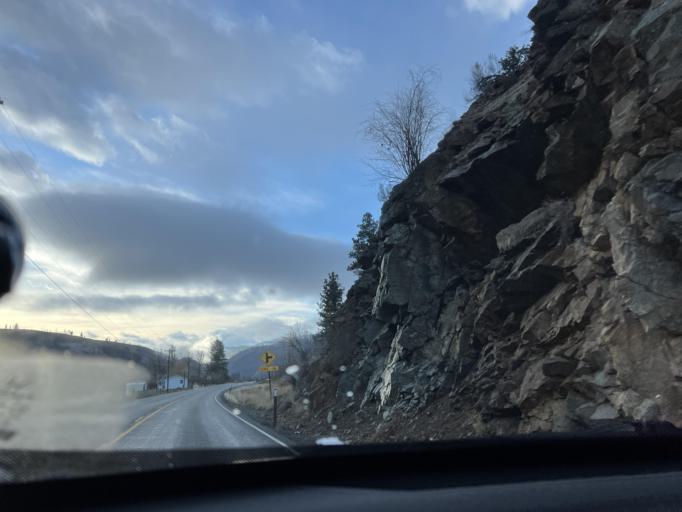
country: US
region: Washington
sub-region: Chelan County
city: Manson
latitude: 48.2324
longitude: -120.1183
